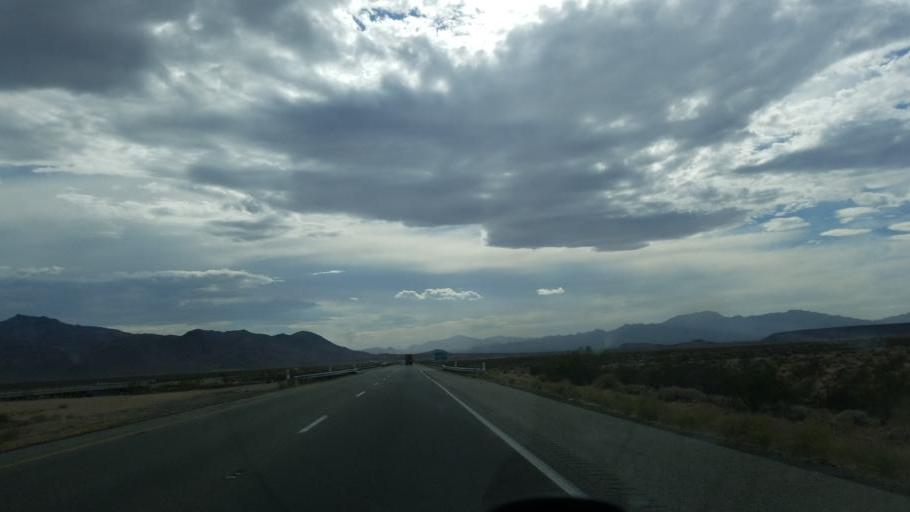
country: US
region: California
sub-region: San Bernardino County
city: Needles
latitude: 34.8037
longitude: -115.2907
